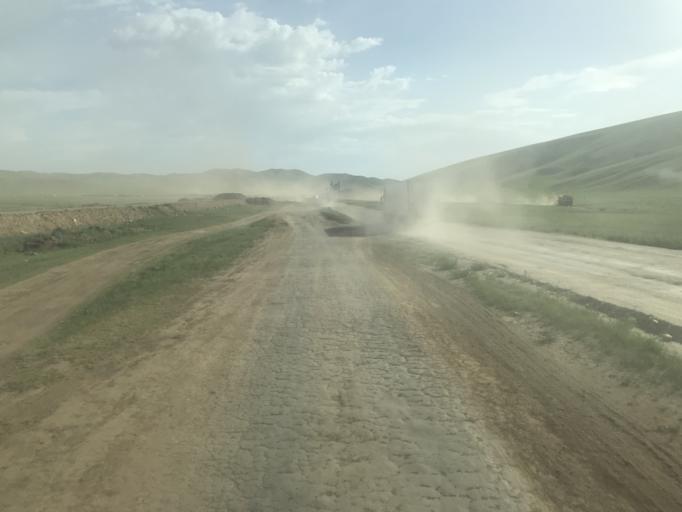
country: MN
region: Central Aimak
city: Bornuur
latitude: 48.6775
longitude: 106.1440
